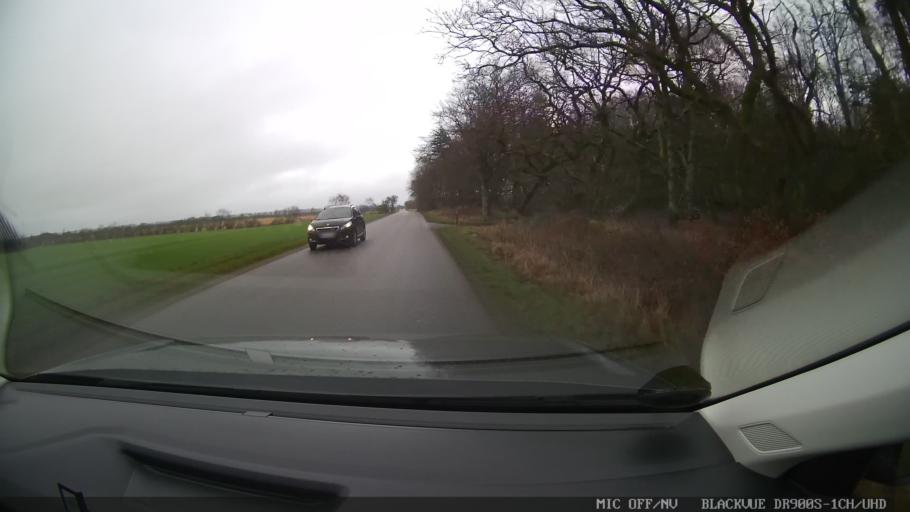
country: DK
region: Central Jutland
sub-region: Viborg Kommune
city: Karup
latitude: 56.3358
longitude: 9.2730
